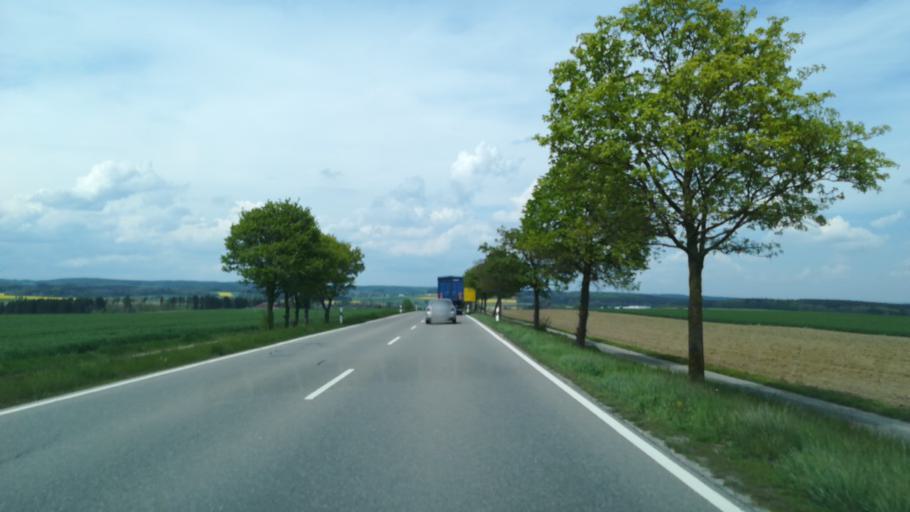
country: DE
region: Baden-Wuerttemberg
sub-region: Freiburg Region
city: Muhlingen
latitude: 47.9509
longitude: 9.0448
